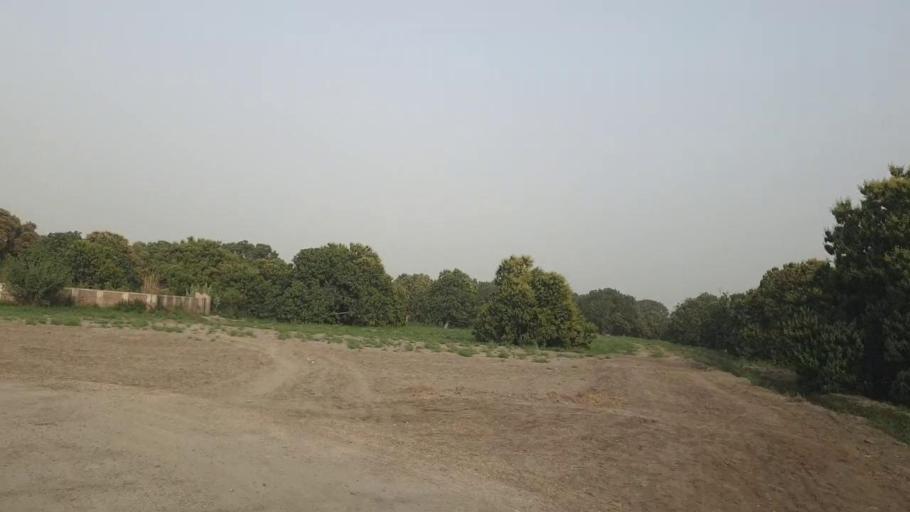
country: PK
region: Sindh
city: Kunri
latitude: 25.0677
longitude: 69.4417
